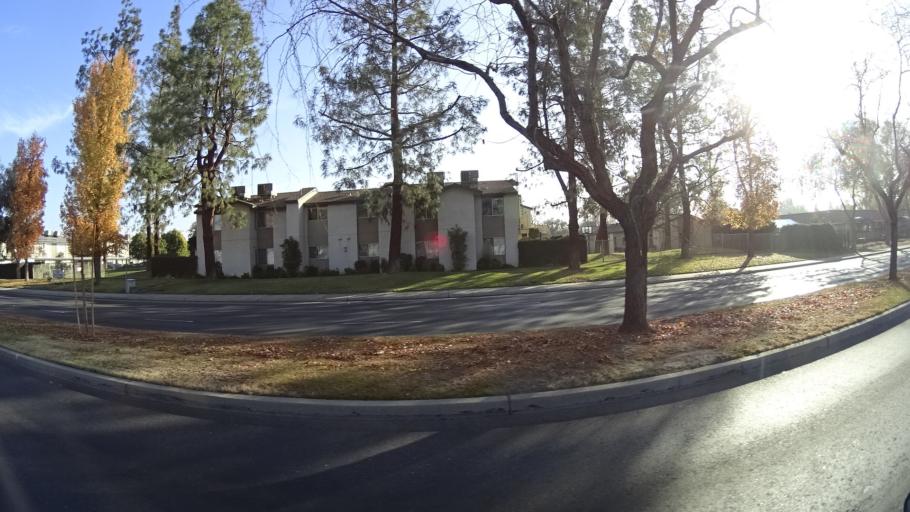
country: US
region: California
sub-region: Kern County
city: Greenacres
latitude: 35.3313
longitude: -119.0923
